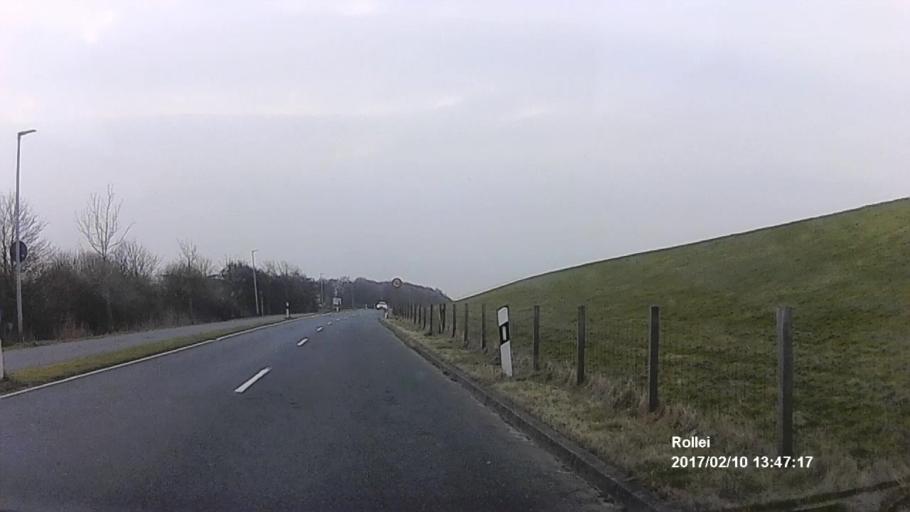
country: DE
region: Lower Saxony
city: Norddeich
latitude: 53.6066
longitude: 7.1410
